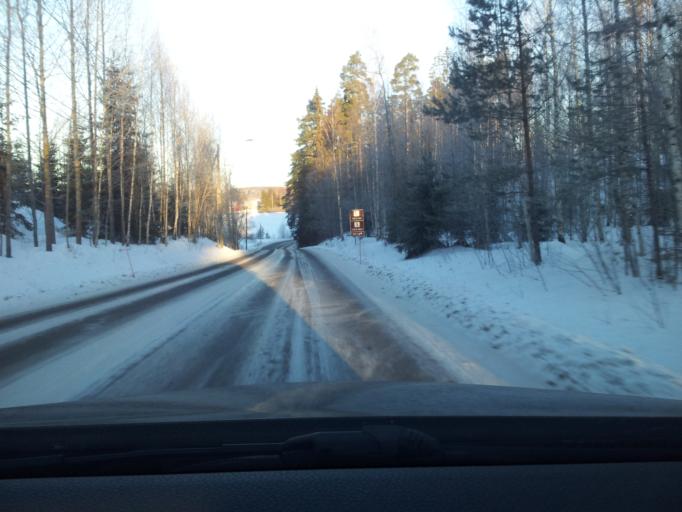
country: FI
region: Uusimaa
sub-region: Helsinki
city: Vihti
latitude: 60.3762
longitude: 24.3601
